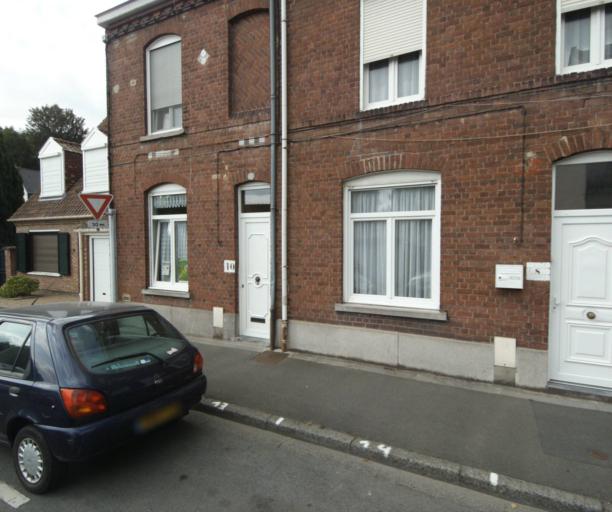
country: FR
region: Nord-Pas-de-Calais
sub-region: Departement du Nord
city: Lys-lez-Lannoy
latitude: 50.6696
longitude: 3.2164
